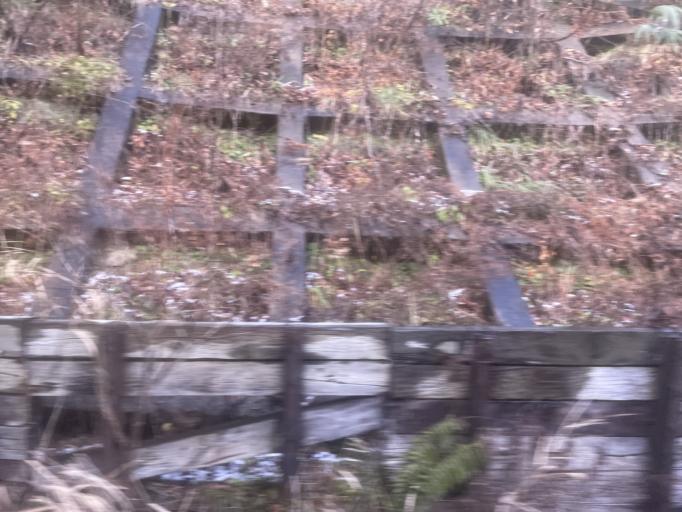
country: JP
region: Aomori
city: Goshogawara
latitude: 41.0776
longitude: 140.5355
